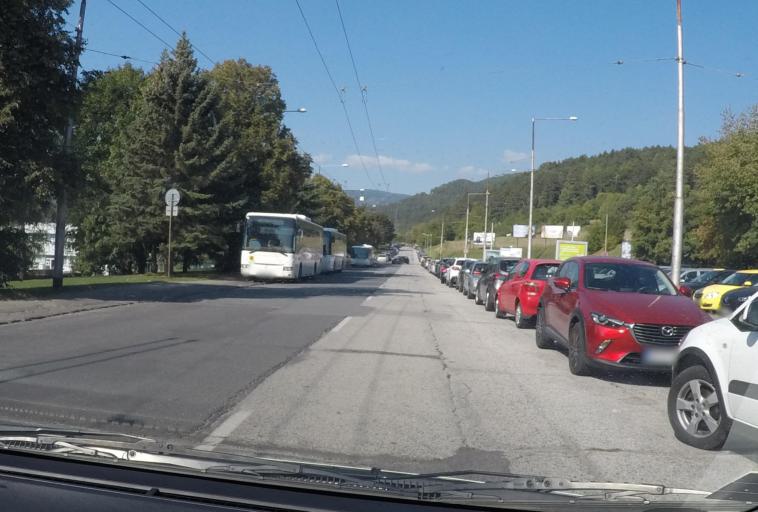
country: SK
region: Banskobystricky
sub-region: Okres Banska Bystrica
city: Banska Bystrica
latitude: 48.7446
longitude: 19.1181
